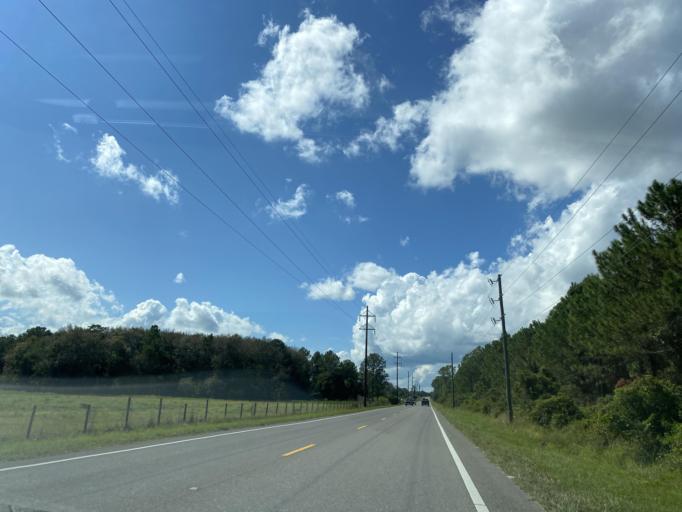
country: US
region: Florida
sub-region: Lake County
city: Umatilla
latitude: 28.9603
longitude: -81.6157
